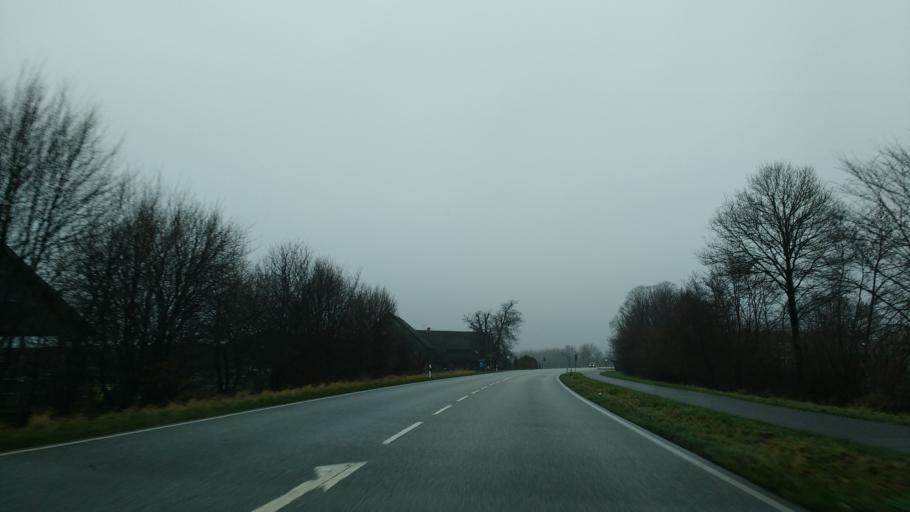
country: DE
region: Schleswig-Holstein
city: Jevenstedt
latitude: 54.2202
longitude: 9.6616
